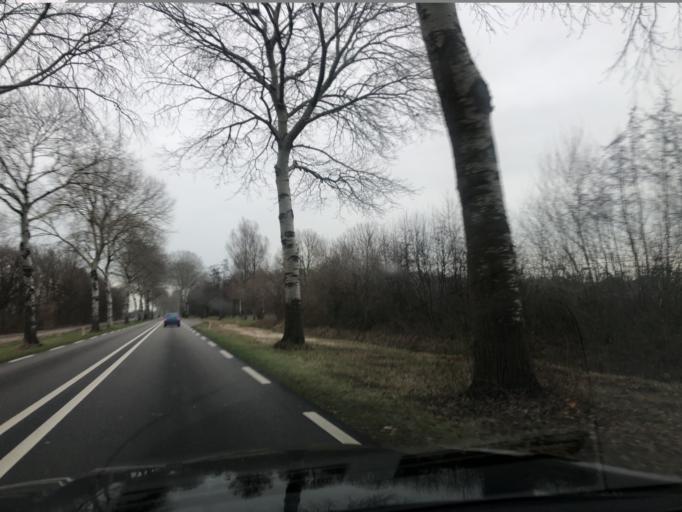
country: NL
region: North Brabant
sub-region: Gemeente Uden
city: Uden
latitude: 51.6742
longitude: 5.6231
